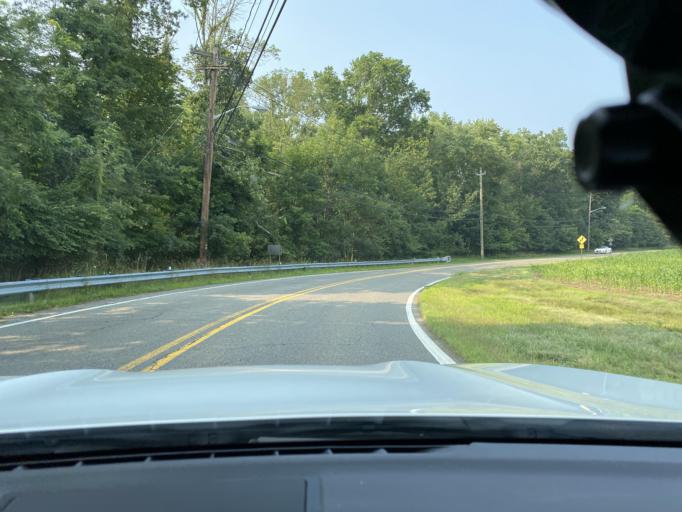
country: US
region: New York
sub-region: Rockland County
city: Airmont
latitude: 41.0919
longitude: -74.1253
